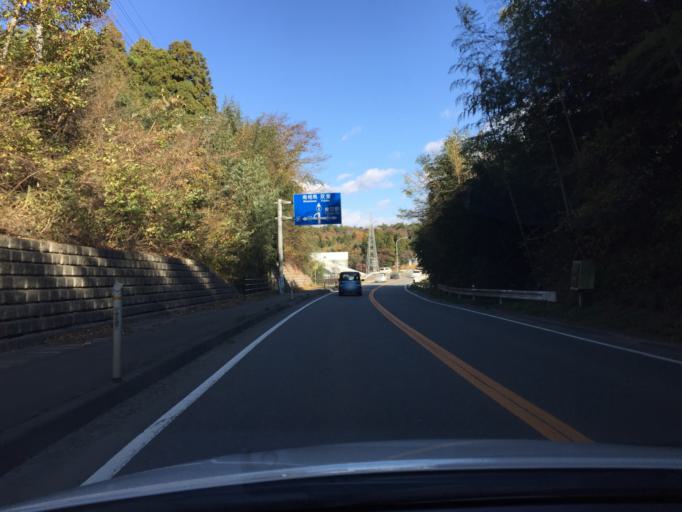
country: JP
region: Fukushima
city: Namie
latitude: 37.2870
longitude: 140.9911
